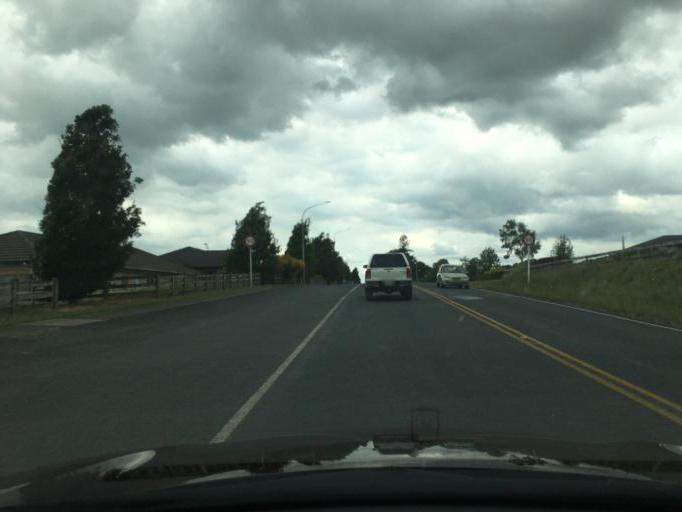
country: NZ
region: Waikato
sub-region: Waipa District
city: Cambridge
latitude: -37.8994
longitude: 175.4596
